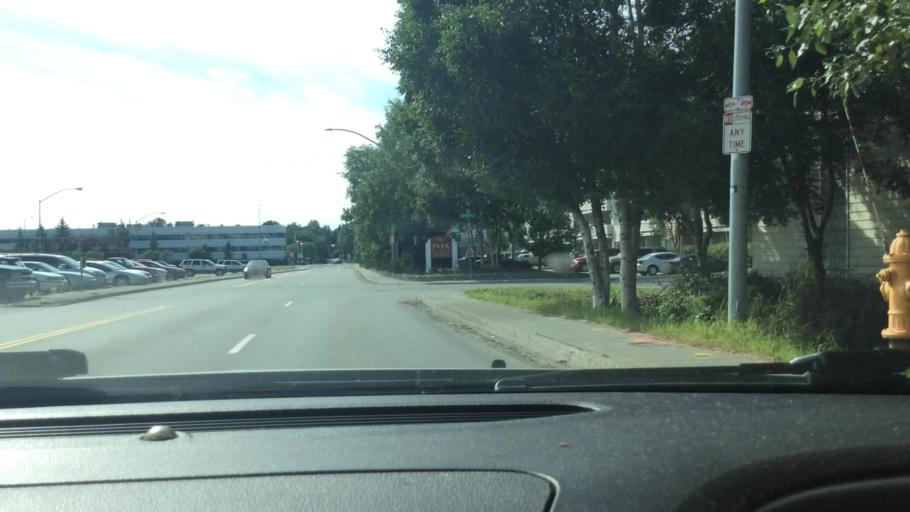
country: US
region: Alaska
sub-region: Anchorage Municipality
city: Anchorage
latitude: 61.2061
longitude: -149.8786
